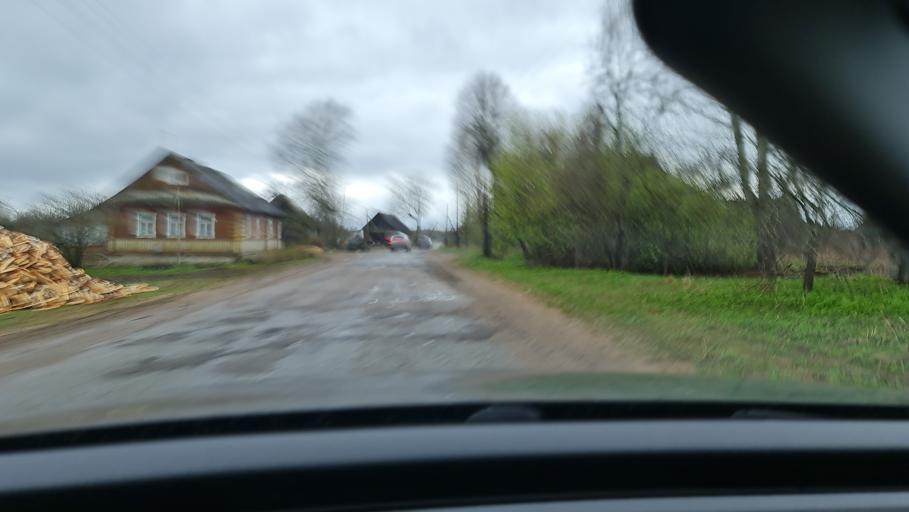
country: RU
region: Novgorod
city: Marevo
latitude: 57.2416
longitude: 32.0471
